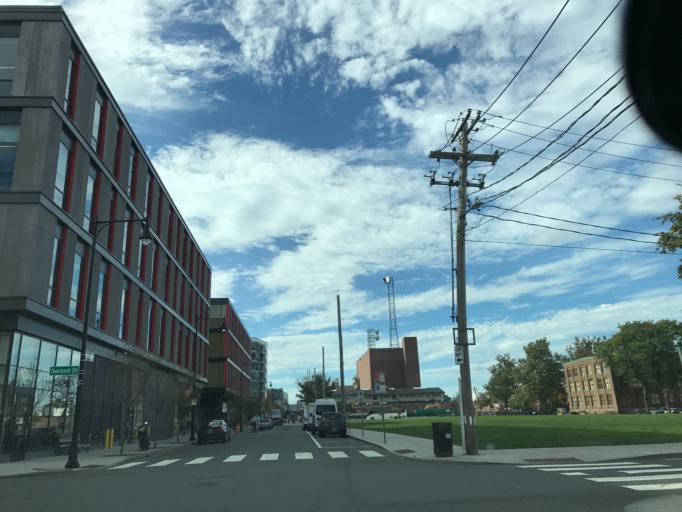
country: US
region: Massachusetts
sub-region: Suffolk County
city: Boston
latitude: 42.3661
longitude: -71.0795
